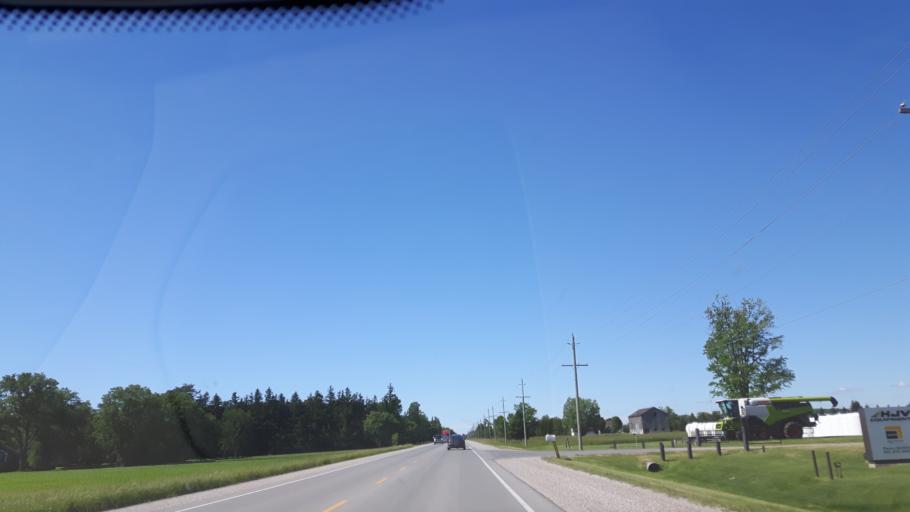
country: CA
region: Ontario
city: South Huron
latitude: 43.4016
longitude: -81.4918
